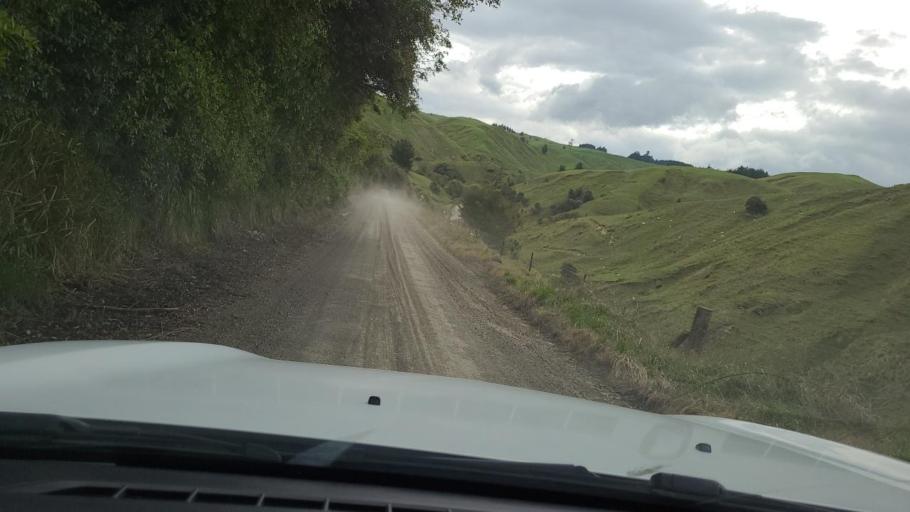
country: NZ
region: Hawke's Bay
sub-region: Napier City
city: Napier
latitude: -39.2771
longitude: 176.8393
